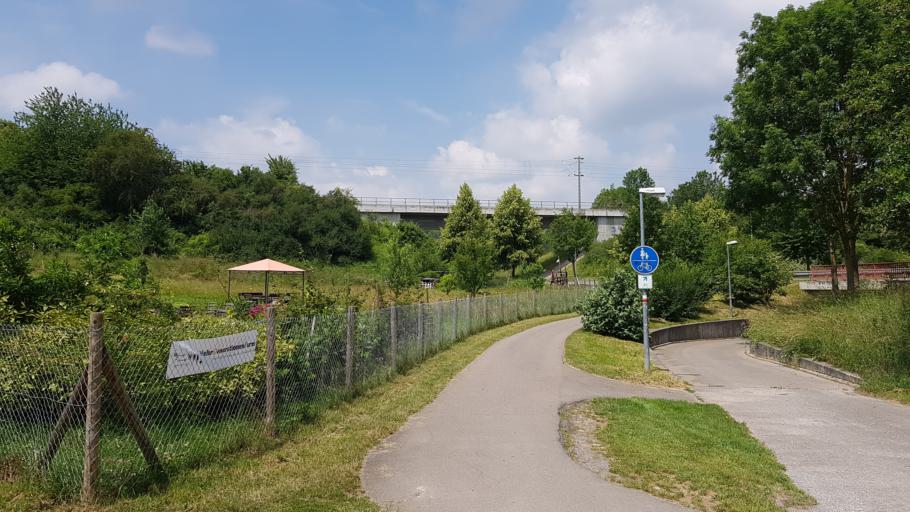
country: DE
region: Baden-Wuerttemberg
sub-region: Regierungsbezirk Stuttgart
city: Weil der Stadt
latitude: 48.7589
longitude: 8.8793
